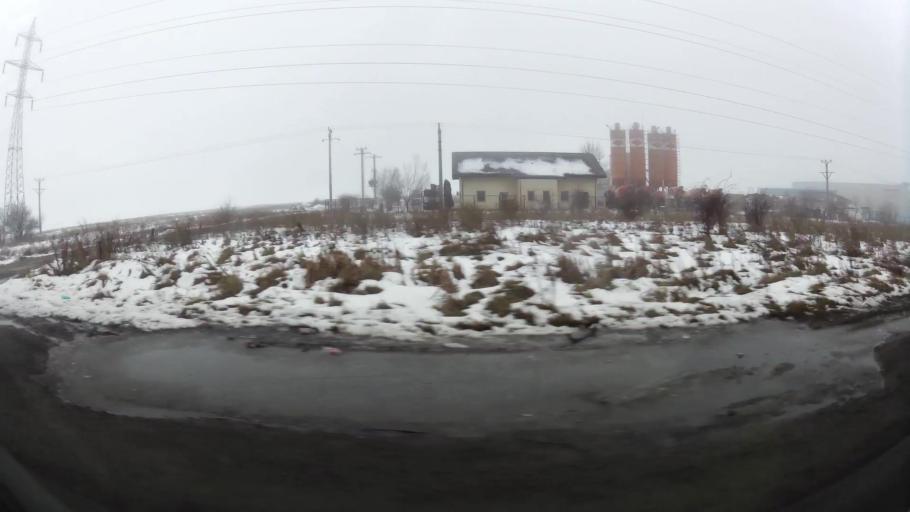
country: RO
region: Ilfov
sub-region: Comuna Chiajna
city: Chiajna
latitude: 44.4297
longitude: 25.9672
